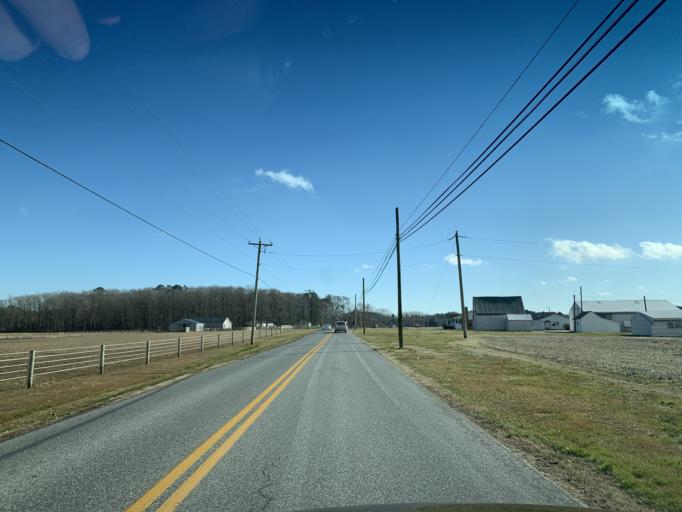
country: US
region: Maryland
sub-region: Worcester County
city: Ocean Pines
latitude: 38.4328
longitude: -75.1796
